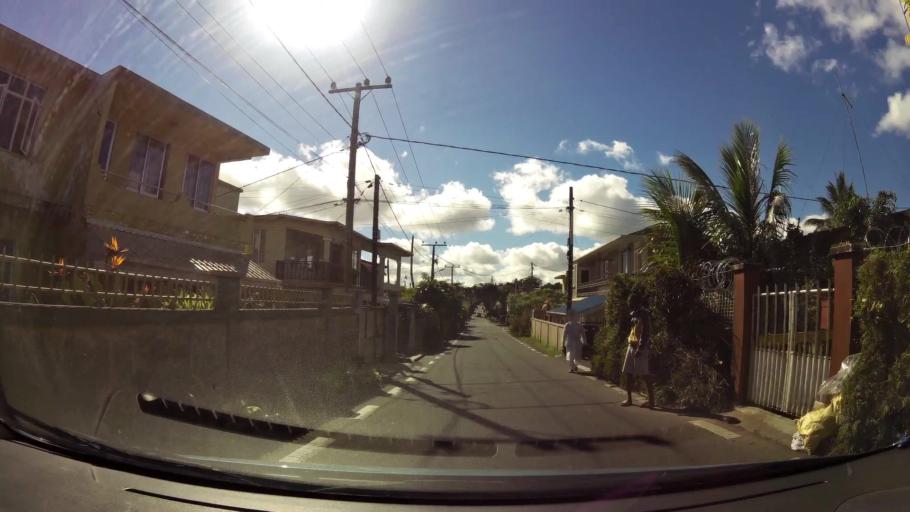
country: MU
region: Plaines Wilhems
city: Vacoas
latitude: -20.3033
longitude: 57.4993
